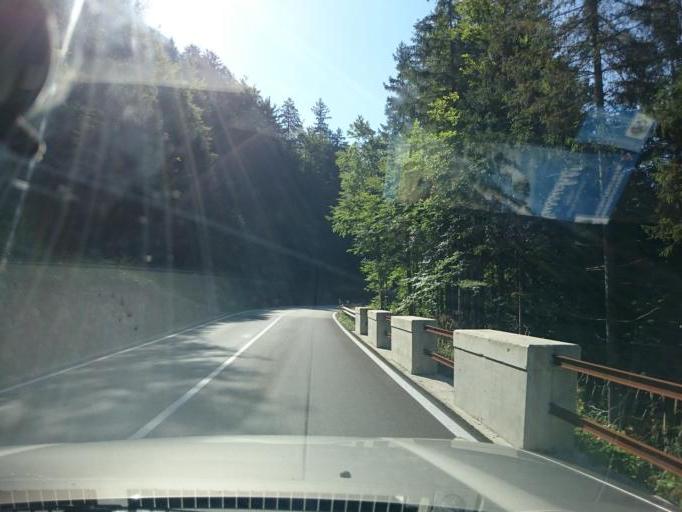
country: IT
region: Friuli Venezia Giulia
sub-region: Provincia di Udine
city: Tarvisio
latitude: 46.4686
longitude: 13.5711
